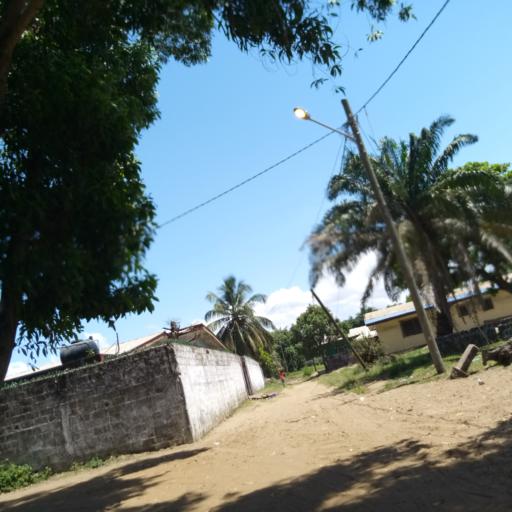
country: LR
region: Montserrado
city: Monrovia
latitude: 6.2350
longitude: -10.6938
